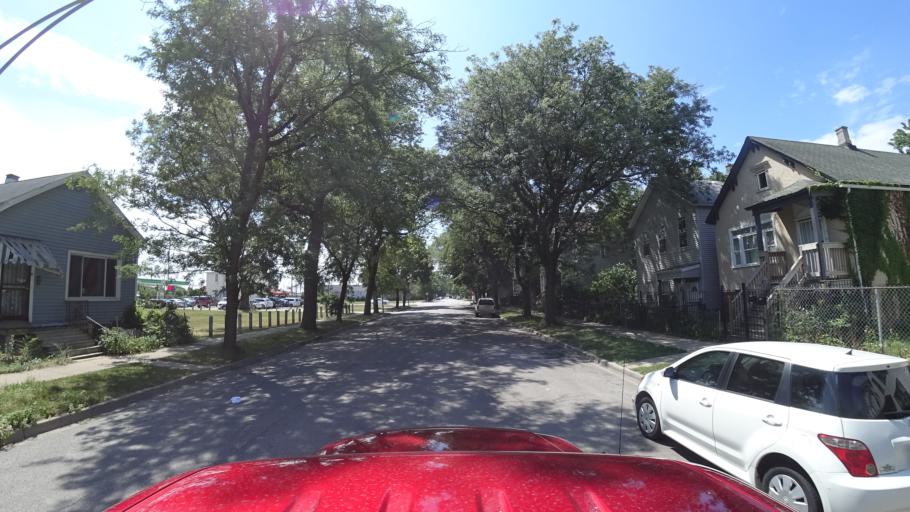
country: US
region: Illinois
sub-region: Cook County
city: Chicago
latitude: 41.8173
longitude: -87.6324
